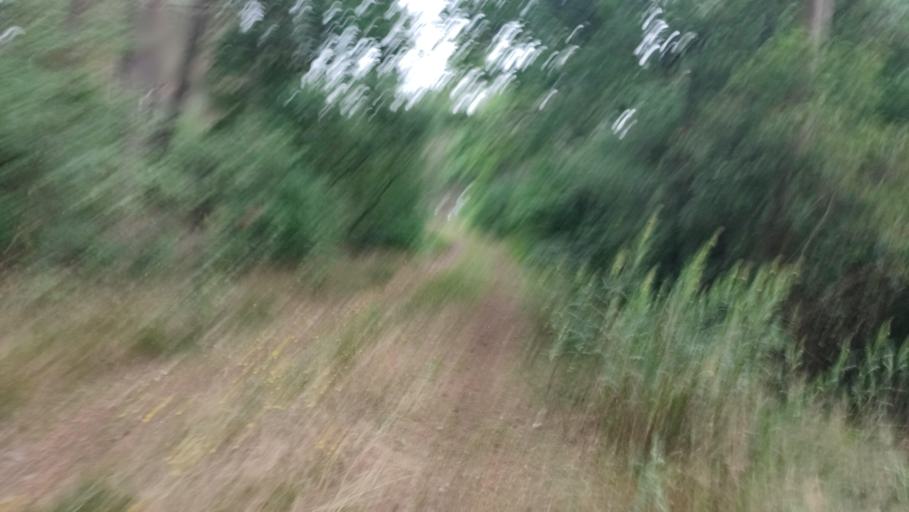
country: DE
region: Lower Saxony
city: Hitzacker
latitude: 53.2019
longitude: 11.0873
